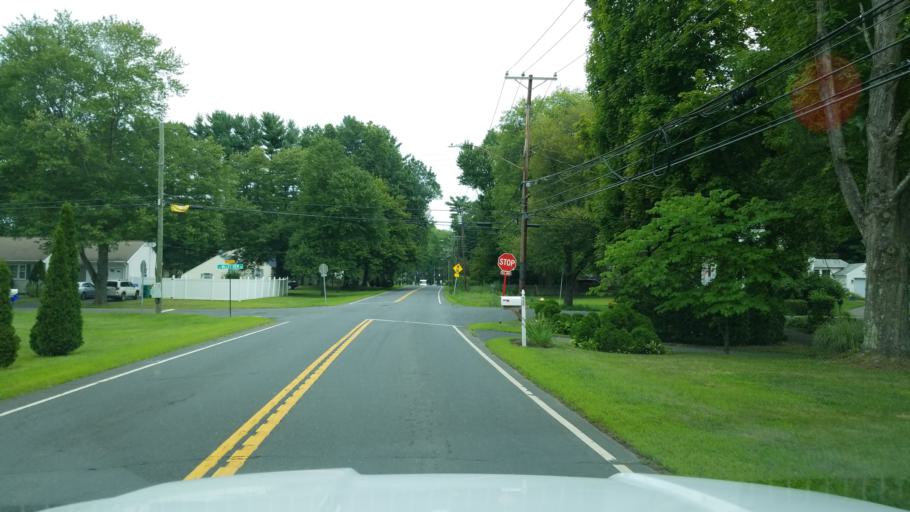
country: US
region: Connecticut
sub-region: Hartford County
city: Blue Hills
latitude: 41.8408
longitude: -72.7457
